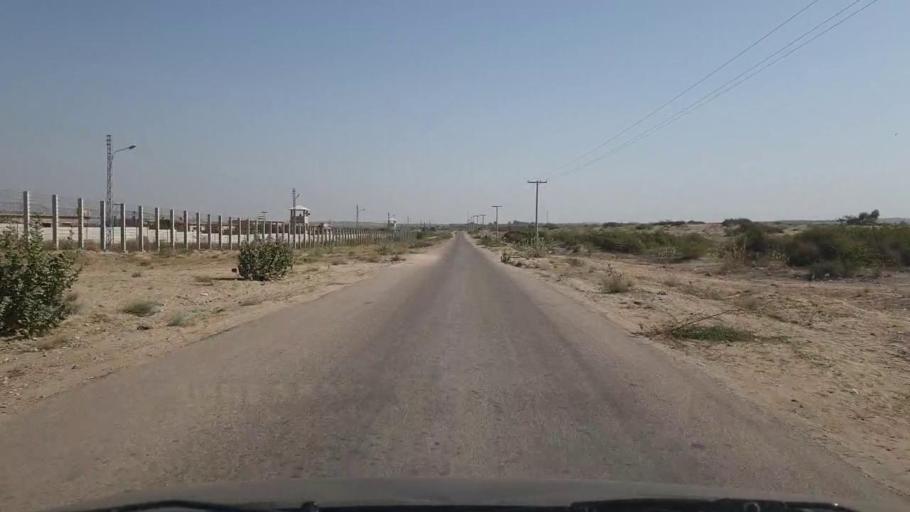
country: PK
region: Sindh
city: Chor
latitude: 25.5160
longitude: 69.8099
